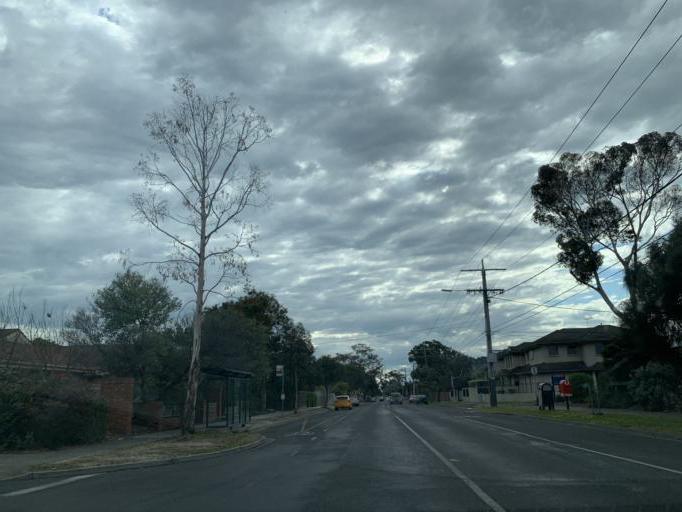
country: AU
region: Victoria
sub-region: Bayside
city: Hampton East
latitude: -37.9351
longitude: 145.0205
